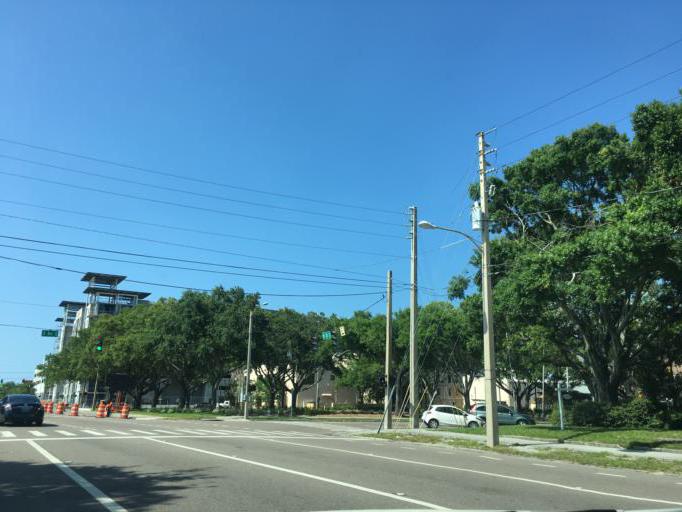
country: US
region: Florida
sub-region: Pinellas County
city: Saint Petersburg
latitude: 27.7682
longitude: -82.6448
